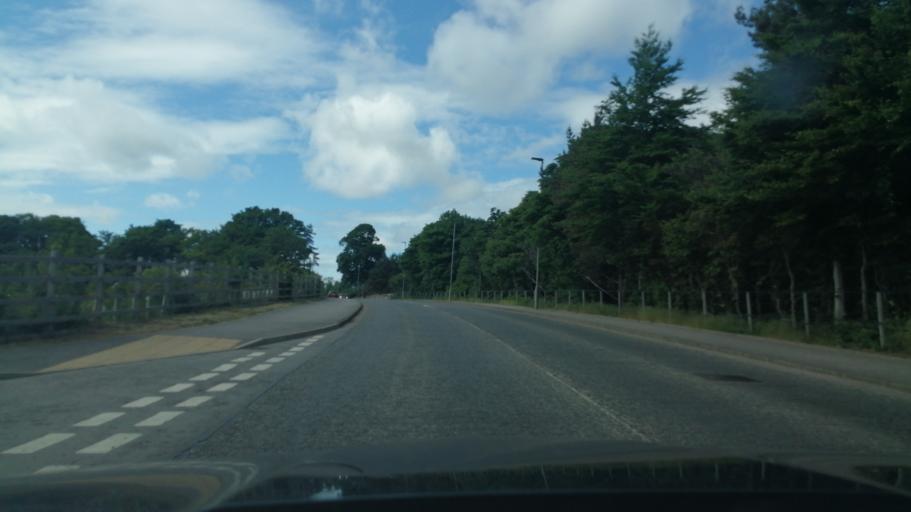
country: GB
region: Scotland
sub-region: Moray
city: Elgin
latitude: 57.6553
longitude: -3.3015
